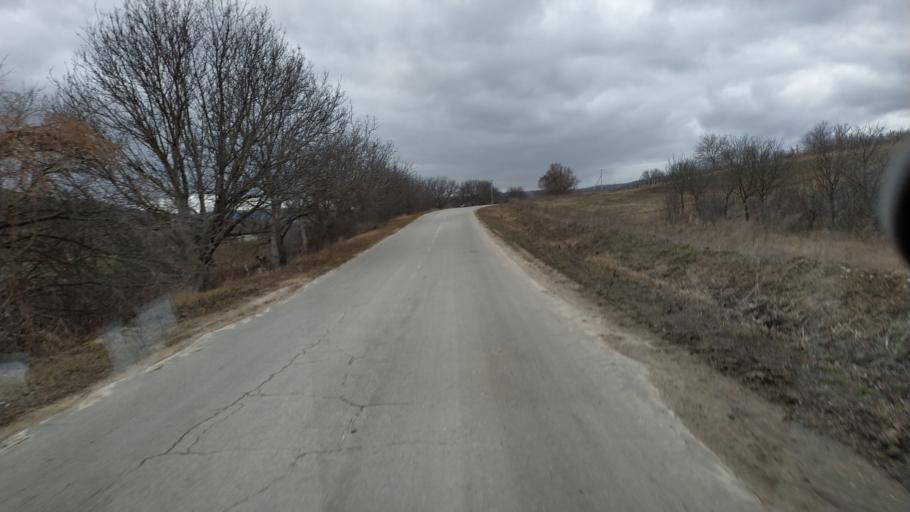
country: MD
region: Calarasi
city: Calarasi
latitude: 47.2434
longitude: 28.1587
